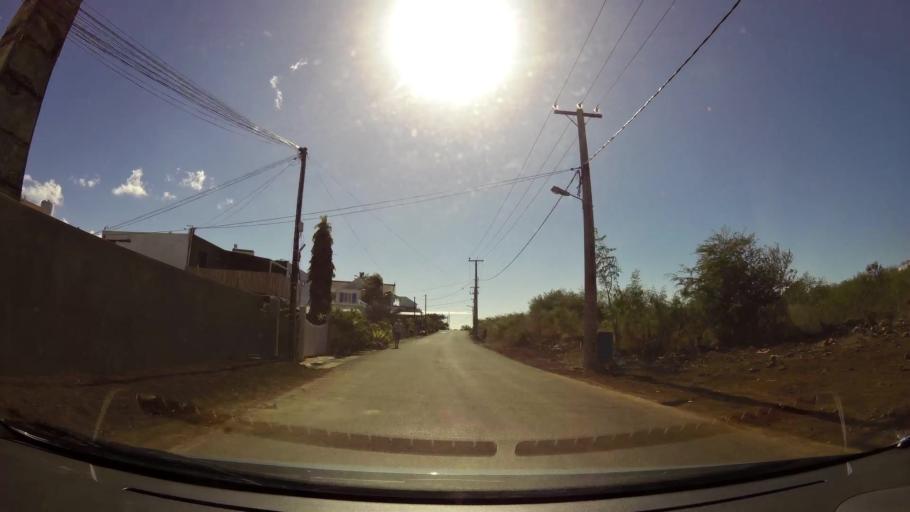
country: MU
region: Black River
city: Flic en Flac
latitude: -20.2726
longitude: 57.3752
